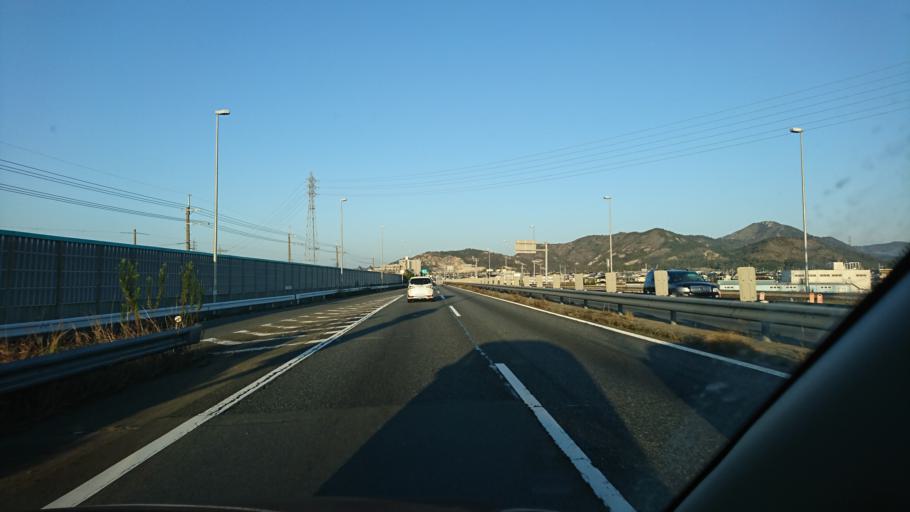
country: JP
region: Hyogo
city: Kakogawacho-honmachi
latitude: 34.7879
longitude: 134.8181
